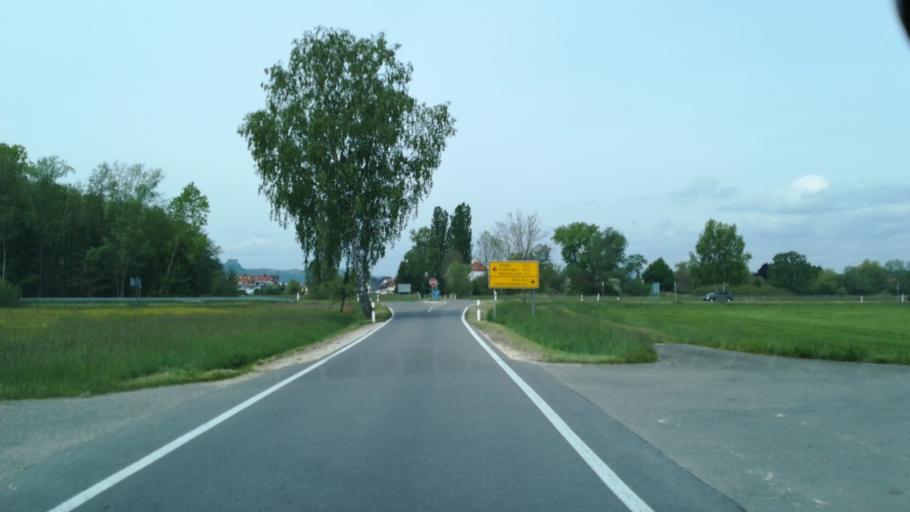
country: DE
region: Baden-Wuerttemberg
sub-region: Freiburg Region
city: Volkertshausen
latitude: 47.7992
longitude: 8.8816
